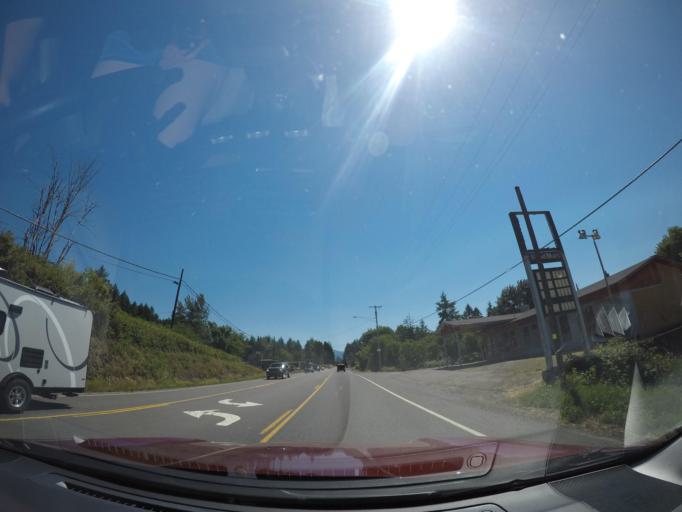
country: US
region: Oregon
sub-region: Linn County
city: Mill City
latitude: 44.7556
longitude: -122.4726
